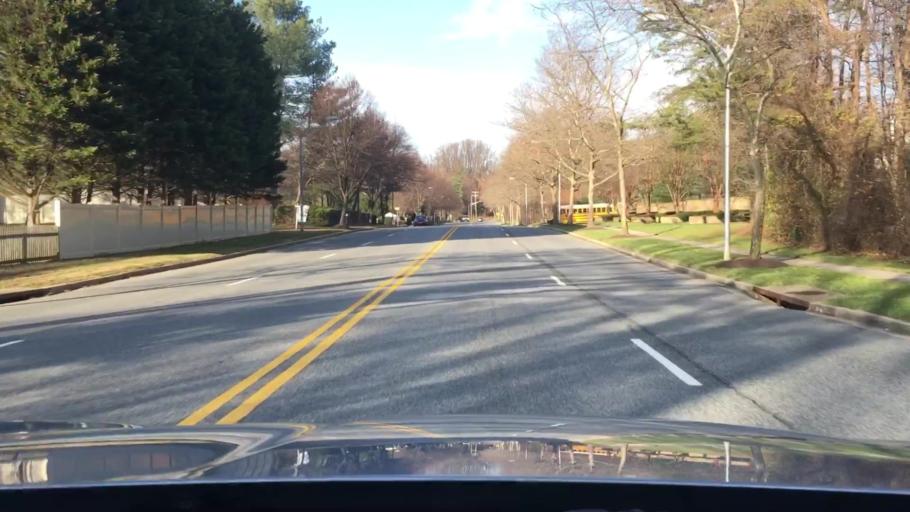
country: US
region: Maryland
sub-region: Prince George's County
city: Glenn Dale
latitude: 38.9746
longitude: -76.7729
